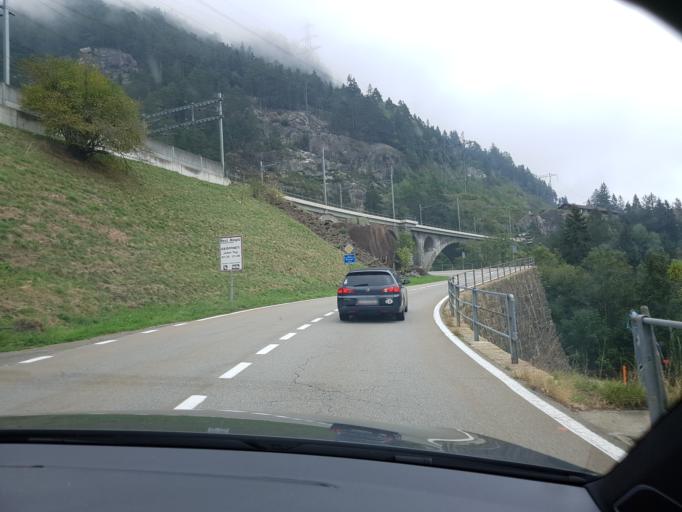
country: CH
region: Uri
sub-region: Uri
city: Andermatt
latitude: 46.7074
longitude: 8.5979
